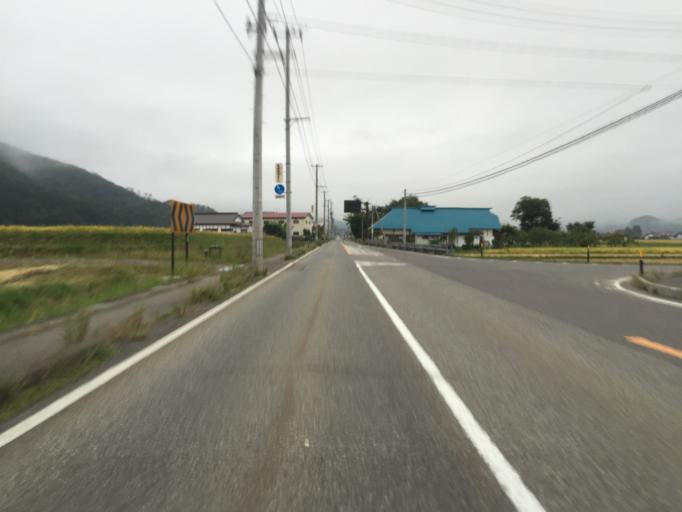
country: JP
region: Fukushima
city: Kitakata
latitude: 37.4536
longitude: 139.9213
